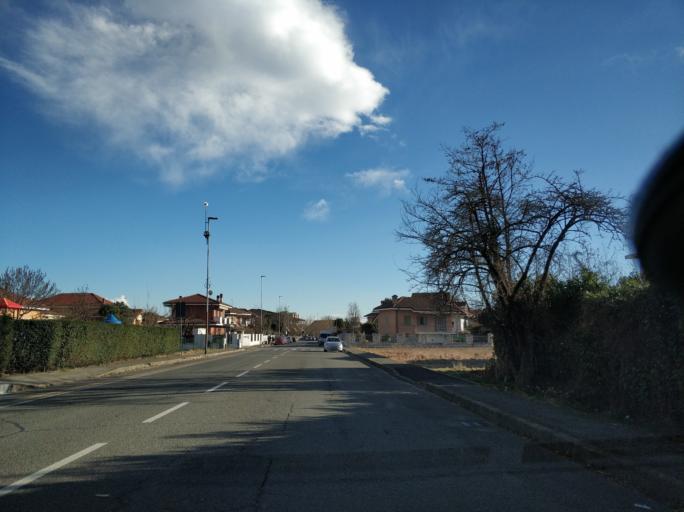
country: IT
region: Piedmont
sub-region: Provincia di Torino
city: Caselle Torinese
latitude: 45.1791
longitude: 7.6379
